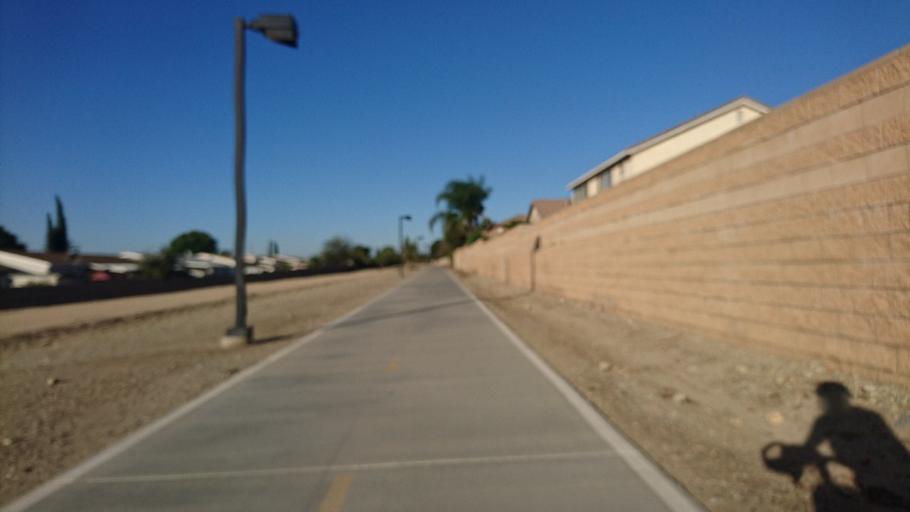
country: US
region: California
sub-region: San Bernardino County
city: Rancho Cucamonga
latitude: 34.1256
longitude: -117.5789
